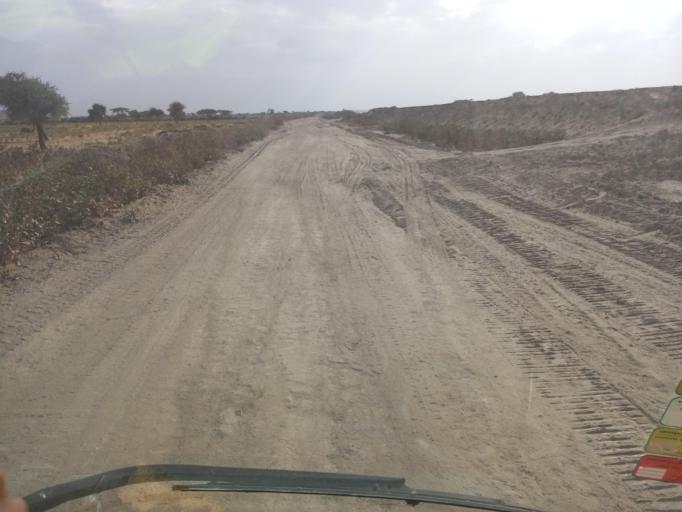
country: ET
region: Oromiya
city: Ziway
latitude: 7.8653
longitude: 38.6710
